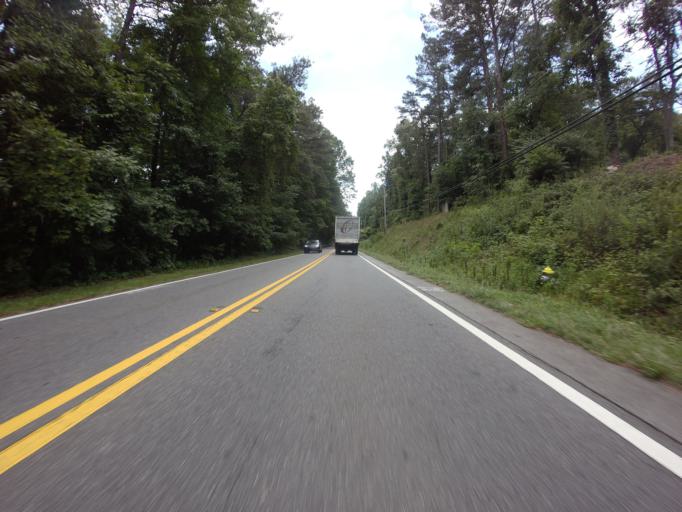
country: US
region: Georgia
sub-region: Fulton County
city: Johns Creek
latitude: 33.9970
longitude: -84.2587
